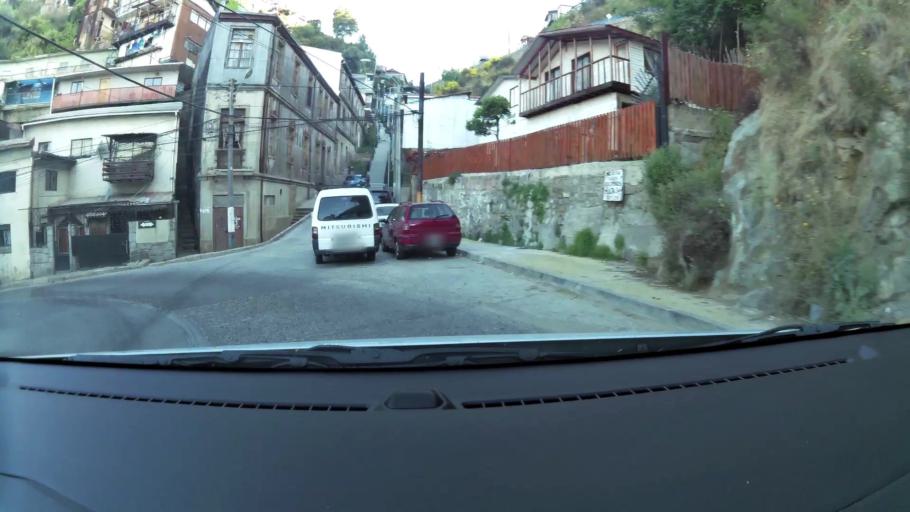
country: CL
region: Valparaiso
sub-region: Provincia de Valparaiso
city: Valparaiso
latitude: -33.0550
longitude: -71.6069
